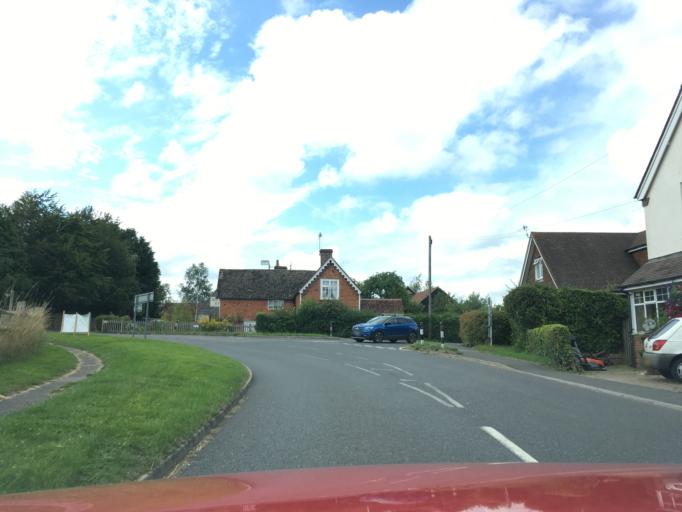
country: GB
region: England
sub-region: East Sussex
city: Crowborough
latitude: 51.1039
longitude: 0.1123
